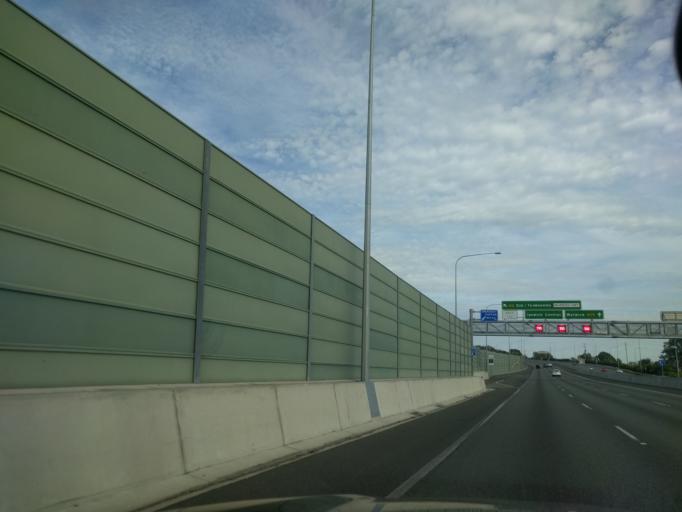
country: AU
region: Queensland
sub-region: Ipswich
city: Redbank
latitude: -27.6013
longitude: 152.8586
